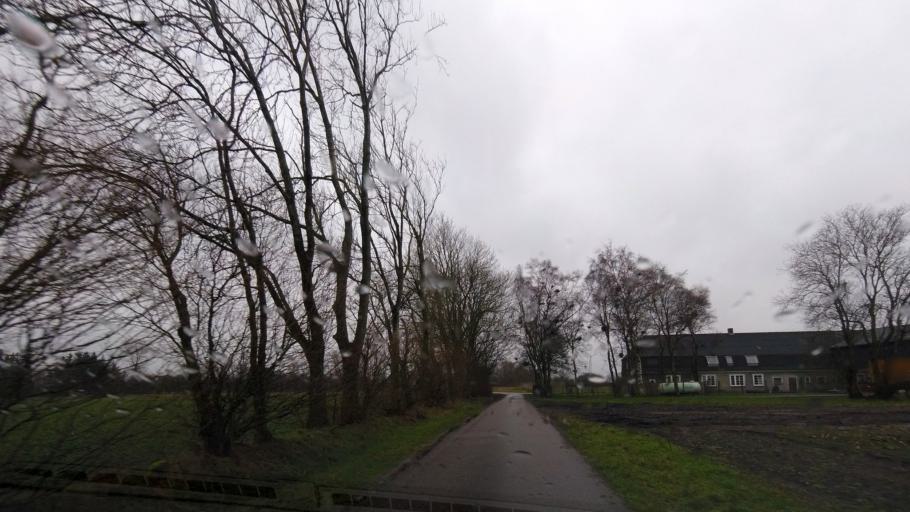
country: DE
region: Schleswig-Holstein
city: Wanderup
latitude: 54.6770
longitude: 9.3072
